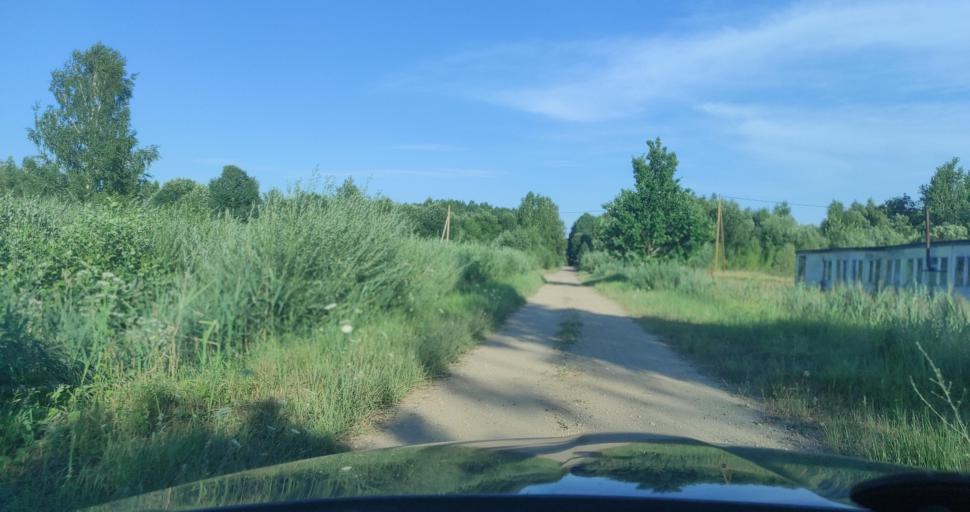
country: LV
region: Skrunda
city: Skrunda
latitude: 56.6755
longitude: 21.9916
